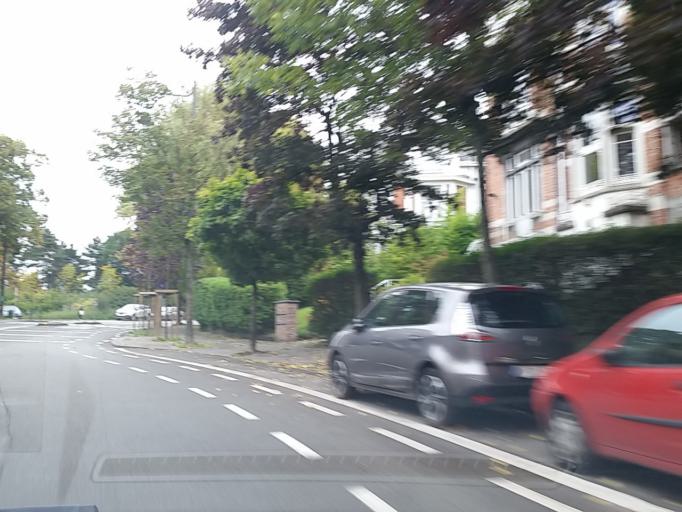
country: BE
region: Brussels Capital
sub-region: Bruxelles-Capitale
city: Brussels
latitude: 50.8211
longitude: 4.3357
